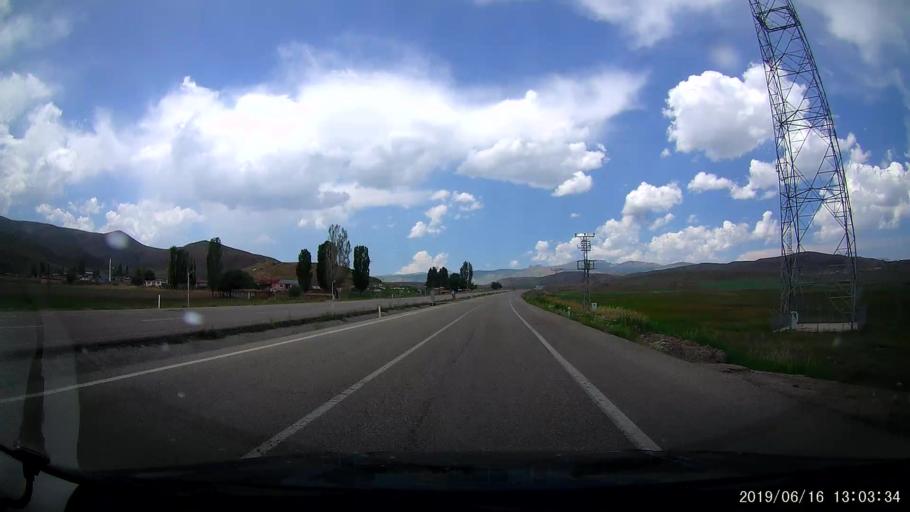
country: TR
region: Agri
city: Sulucem
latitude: 39.5828
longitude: 43.7878
